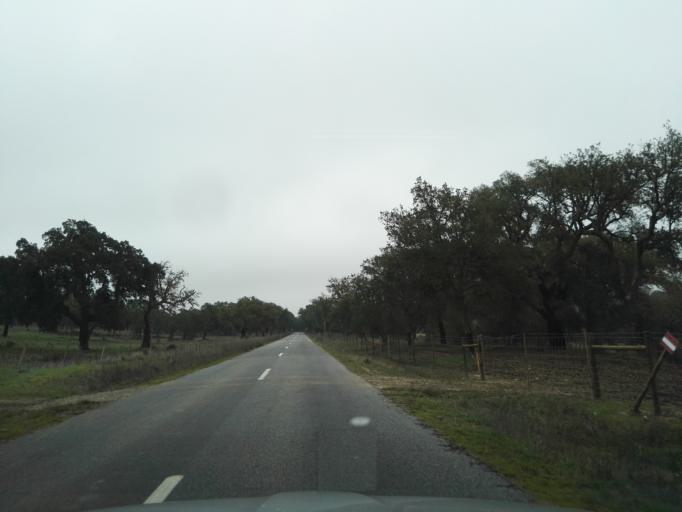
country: PT
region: Evora
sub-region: Vendas Novas
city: Vendas Novas
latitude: 38.7670
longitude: -8.3836
